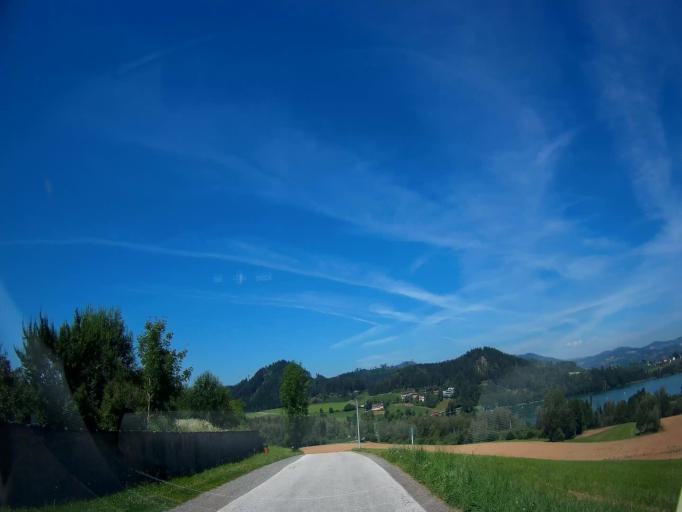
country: AT
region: Carinthia
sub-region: Politischer Bezirk Sankt Veit an der Glan
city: St. Georgen am Laengsee
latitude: 46.7820
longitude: 14.4310
